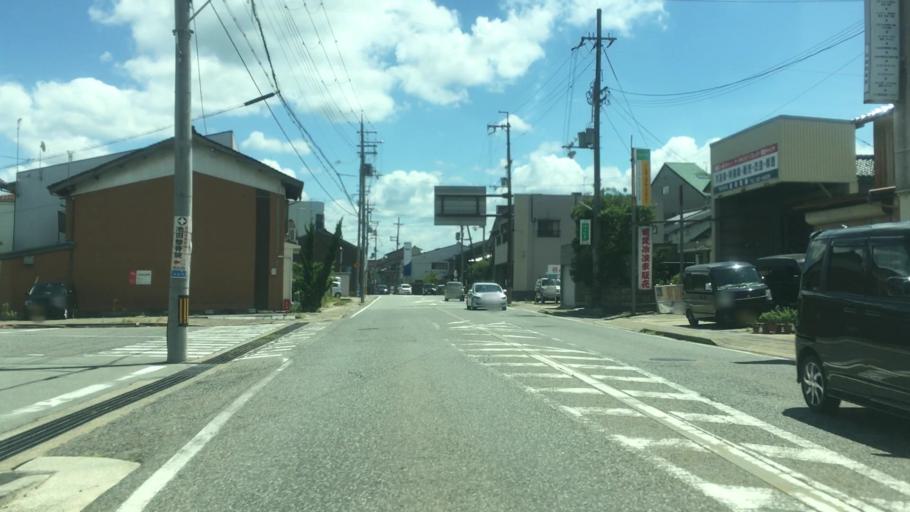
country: JP
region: Hyogo
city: Toyooka
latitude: 35.5400
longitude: 134.8241
